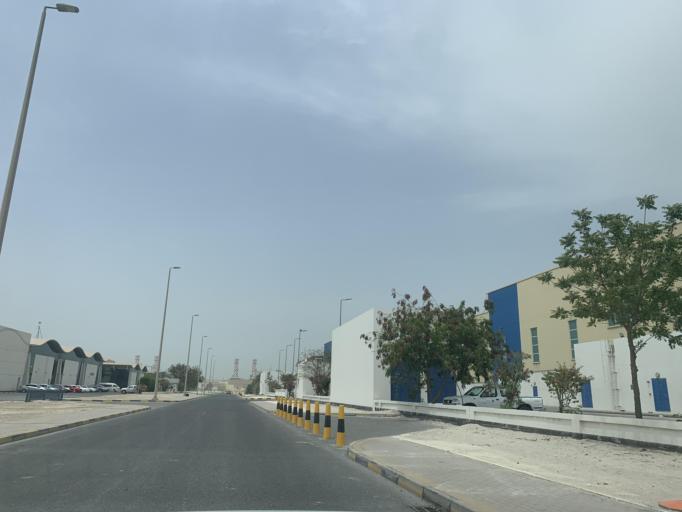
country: BH
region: Muharraq
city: Al Hadd
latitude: 26.2181
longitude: 50.6707
